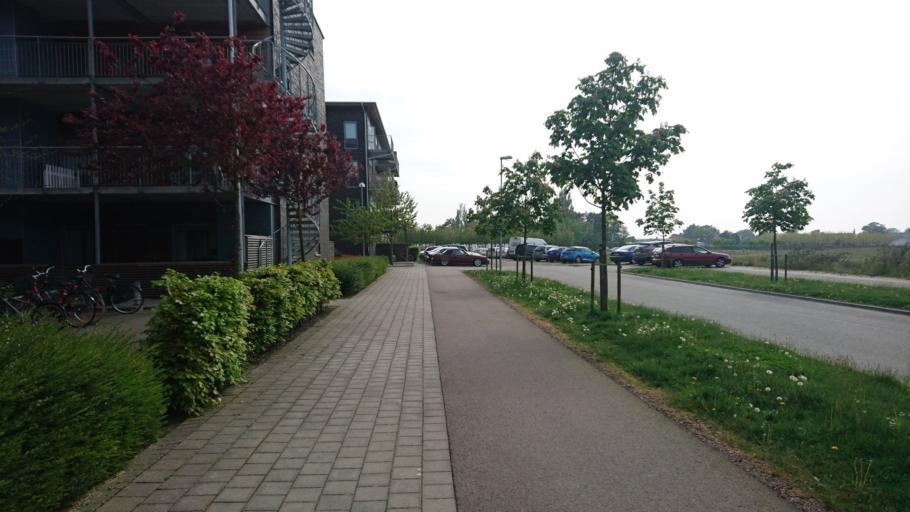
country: SE
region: Skane
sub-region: Malmo
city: Bunkeflostrand
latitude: 55.5606
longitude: 12.9305
